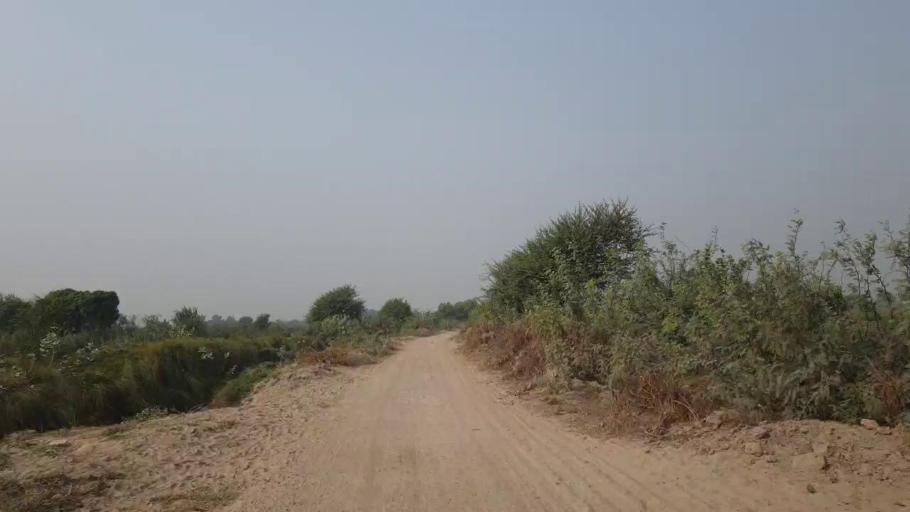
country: PK
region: Sindh
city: Tando Muhammad Khan
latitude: 25.1925
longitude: 68.5783
